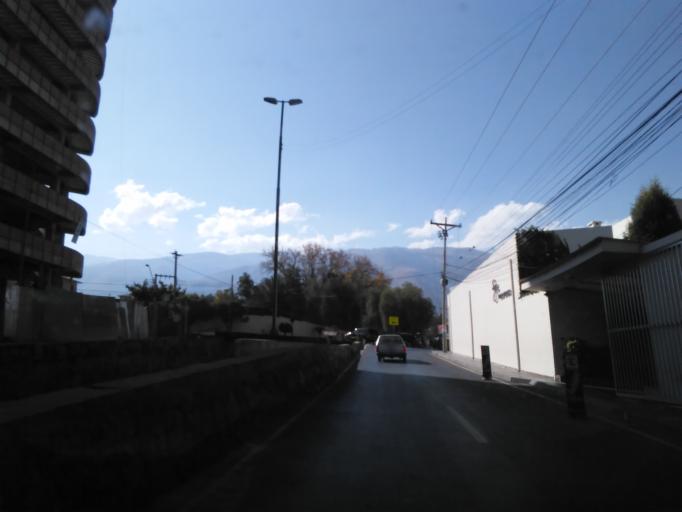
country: BO
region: Cochabamba
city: Cochabamba
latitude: -17.3688
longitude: -66.1681
